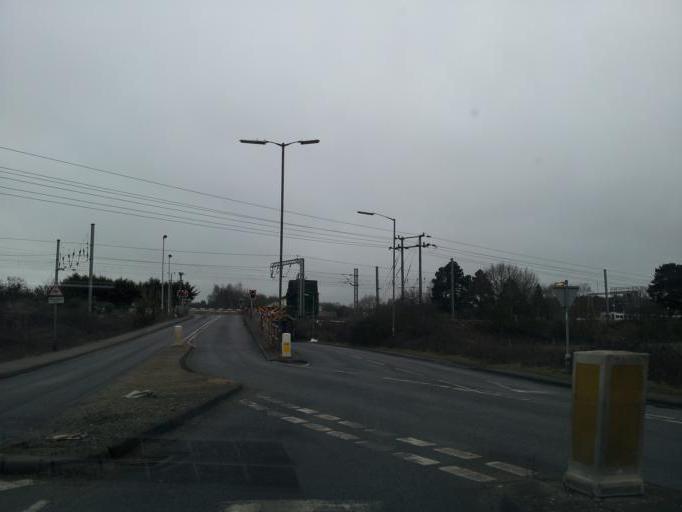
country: GB
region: England
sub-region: Essex
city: Manningtree
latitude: 51.9504
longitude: 1.0488
